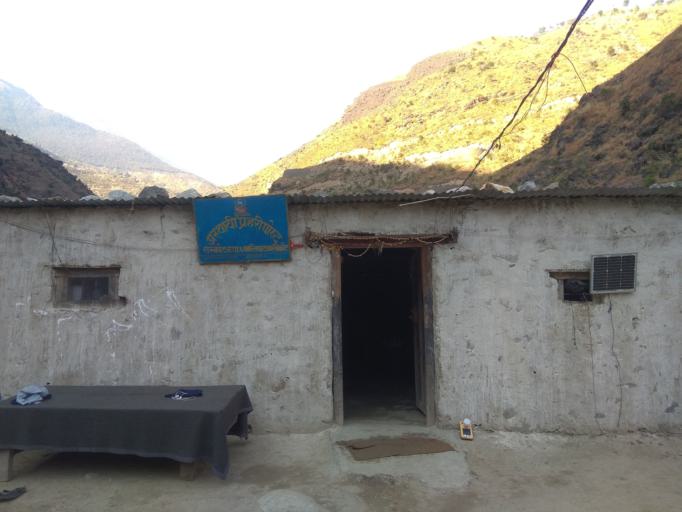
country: NP
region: Far Western
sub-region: Seti Zone
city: Achham
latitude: 29.2241
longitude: 81.6272
